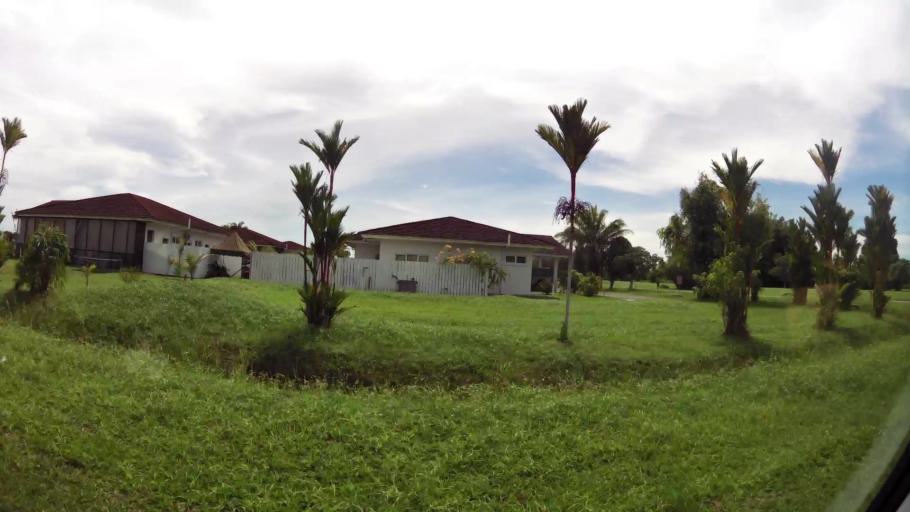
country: BN
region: Belait
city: Seria
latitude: 4.6039
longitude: 114.3175
